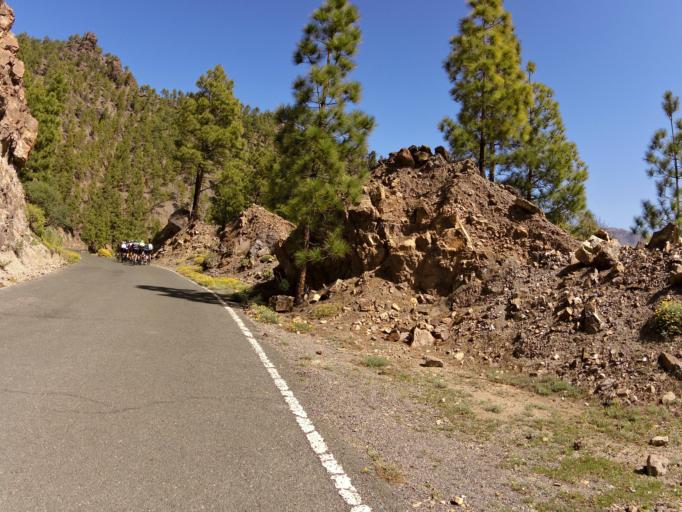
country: ES
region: Canary Islands
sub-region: Provincia de Las Palmas
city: Tejeda
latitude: 27.9384
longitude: -15.6379
